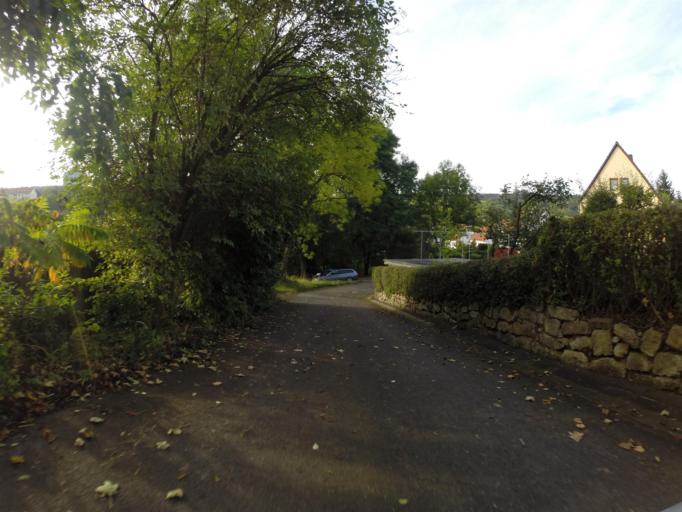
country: DE
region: Thuringia
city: Jena
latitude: 50.9563
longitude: 11.6090
